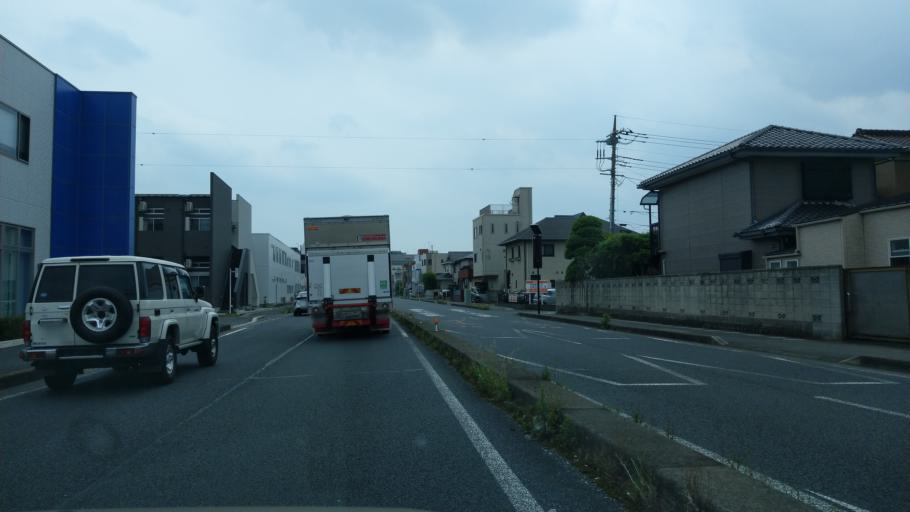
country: JP
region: Saitama
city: Ageoshimo
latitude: 35.9454
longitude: 139.6114
